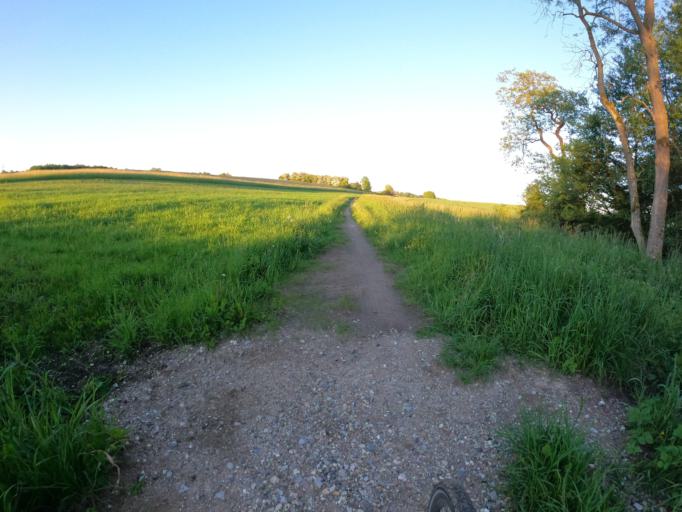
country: DK
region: Zealand
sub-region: Greve Kommune
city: Tune
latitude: 55.6263
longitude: 12.2259
